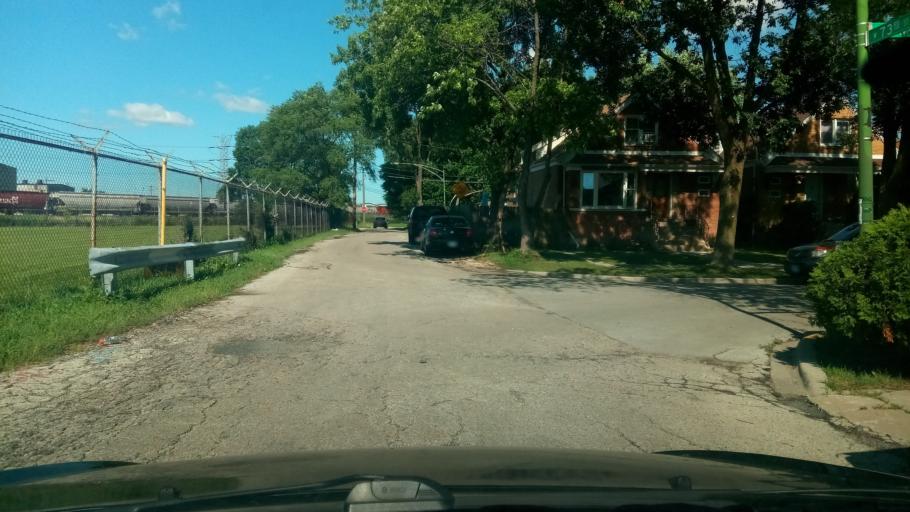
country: US
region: Illinois
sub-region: Cook County
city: Hometown
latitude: 41.7608
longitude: -87.7170
